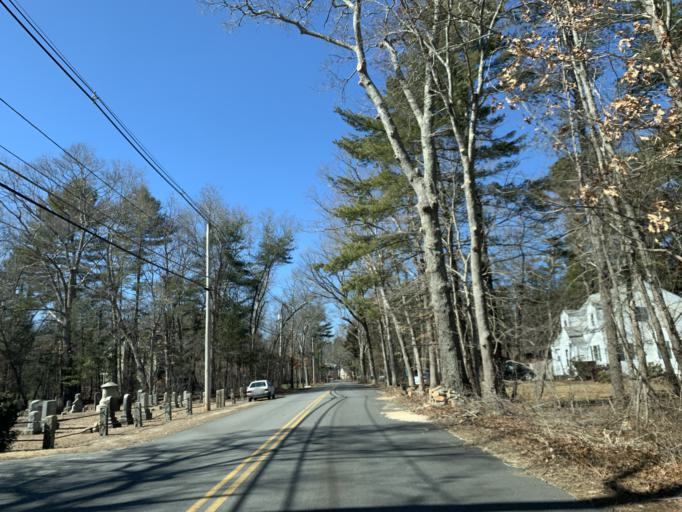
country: US
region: Massachusetts
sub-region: Bristol County
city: Norton
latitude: 41.9447
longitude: -71.1675
